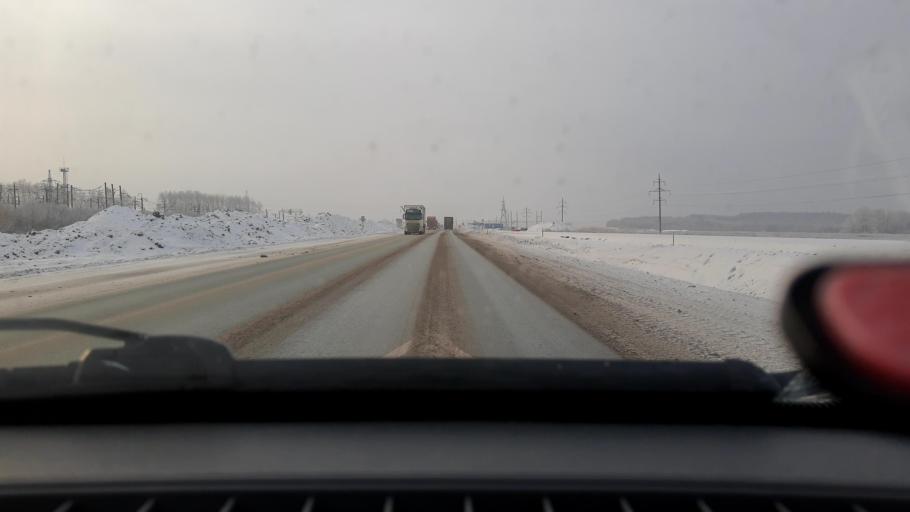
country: RU
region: Bashkortostan
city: Kabakovo
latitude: 54.7038
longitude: 56.2187
